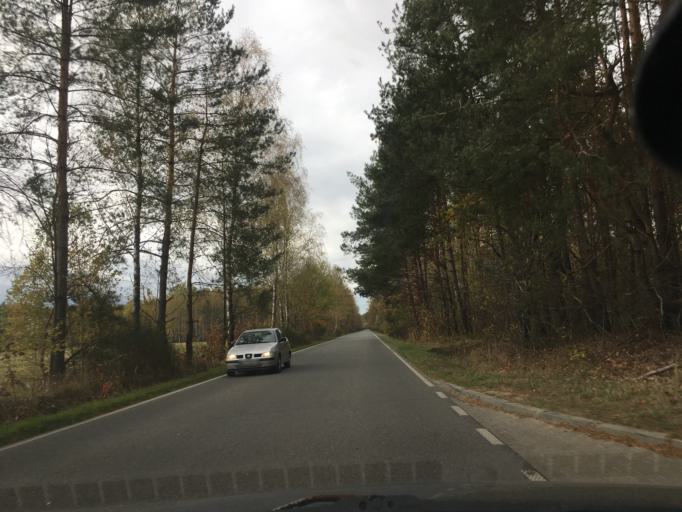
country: PL
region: Masovian Voivodeship
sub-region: Powiat zyrardowski
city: Radziejowice
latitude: 51.9670
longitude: 20.5998
